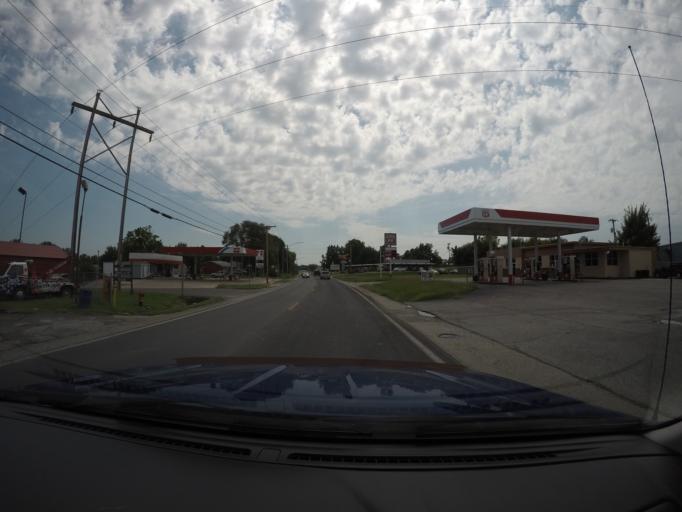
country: US
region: Missouri
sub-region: Lafayette County
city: Lexington
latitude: 39.1674
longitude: -93.8787
